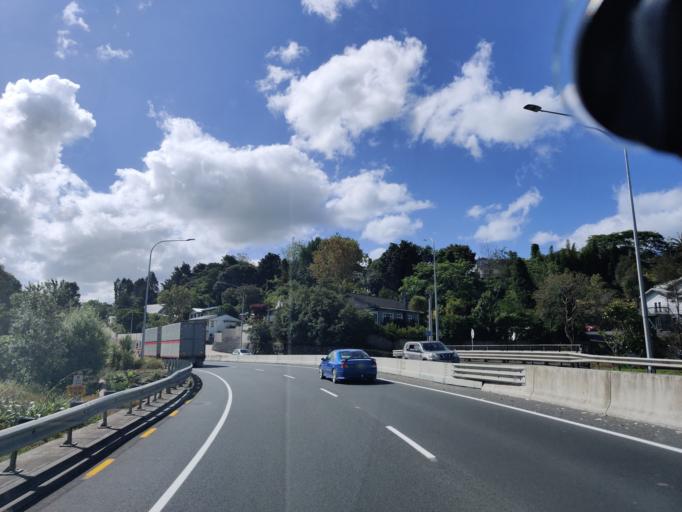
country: NZ
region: Northland
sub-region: Whangarei
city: Whangarei
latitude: -35.7129
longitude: 174.3163
